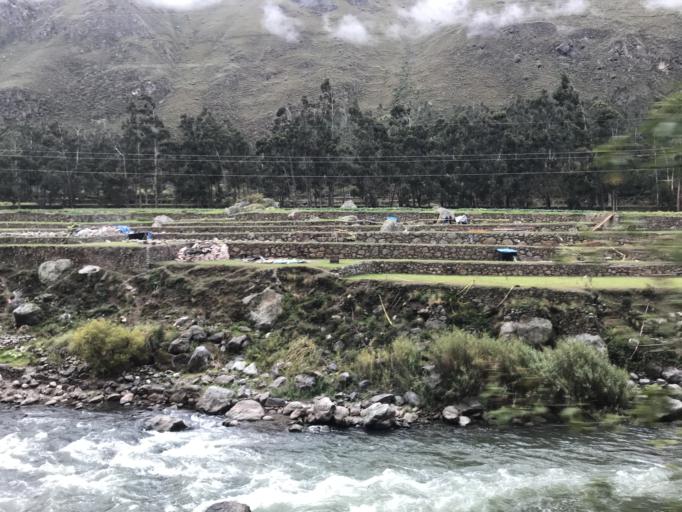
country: PE
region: Cusco
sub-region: Provincia de La Convencion
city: Santa Teresa
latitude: -13.2241
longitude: -72.4410
